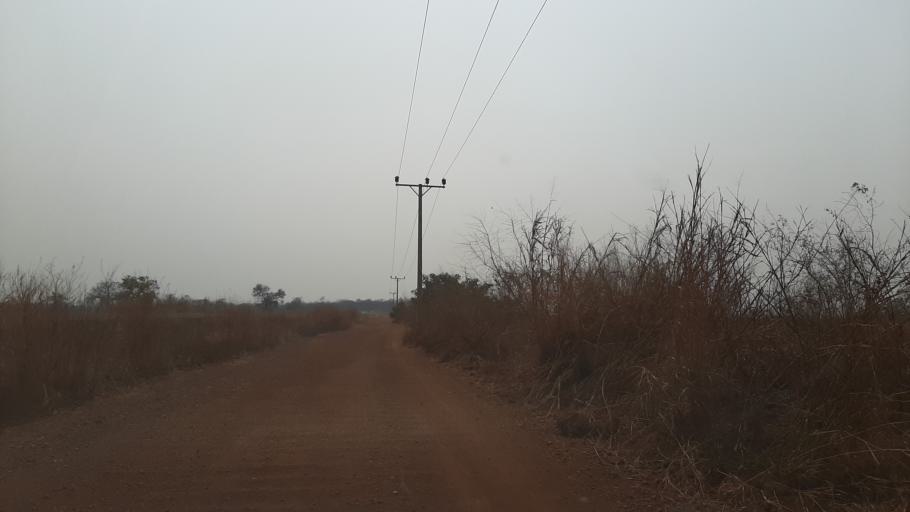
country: ET
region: Gambela
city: Gambela
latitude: 8.1435
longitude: 34.4316
